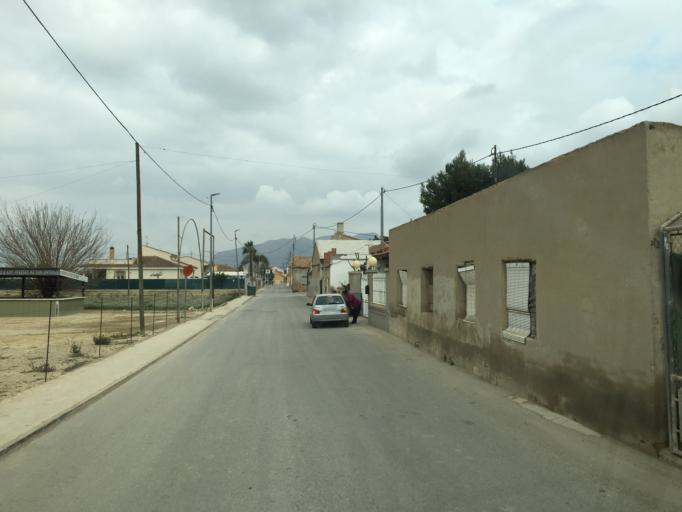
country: ES
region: Murcia
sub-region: Murcia
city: Beniel
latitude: 38.0365
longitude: -0.9865
